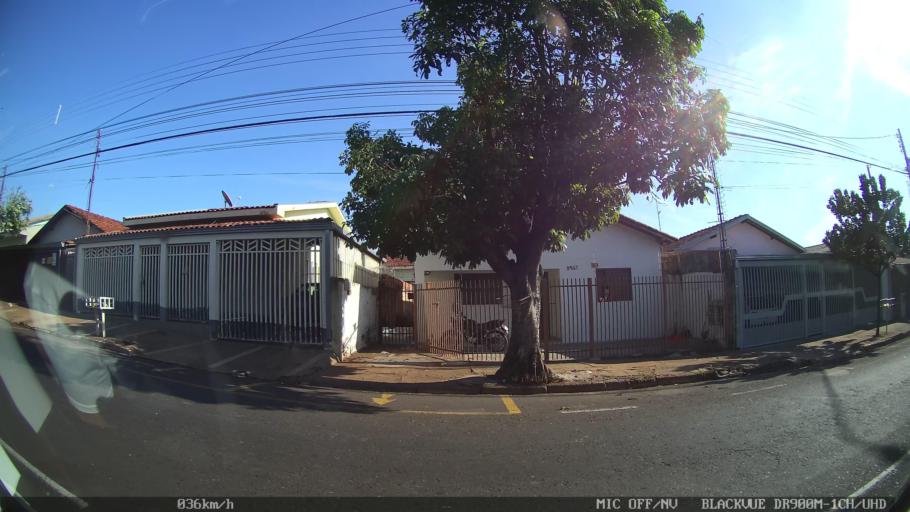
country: BR
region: Sao Paulo
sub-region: Sao Jose Do Rio Preto
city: Sao Jose do Rio Preto
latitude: -20.7779
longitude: -49.4016
